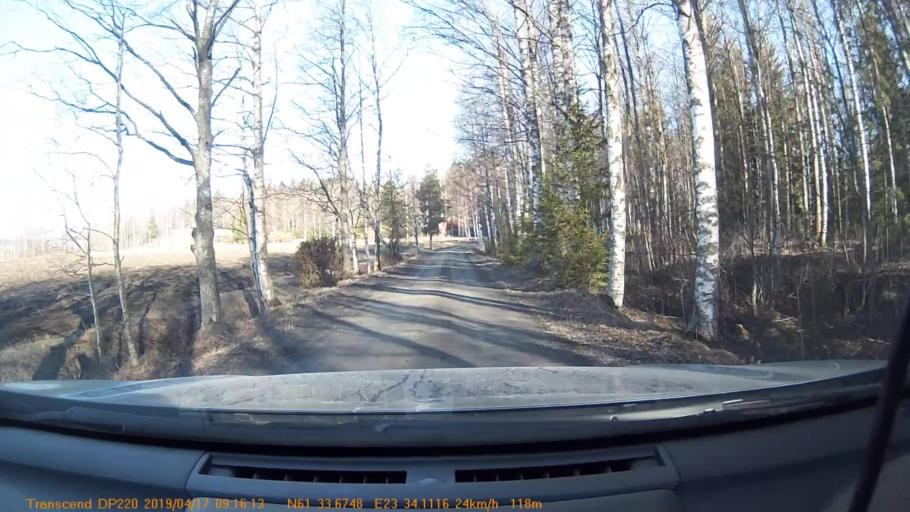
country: FI
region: Pirkanmaa
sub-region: Tampere
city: Yloejaervi
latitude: 61.5612
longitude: 23.5685
